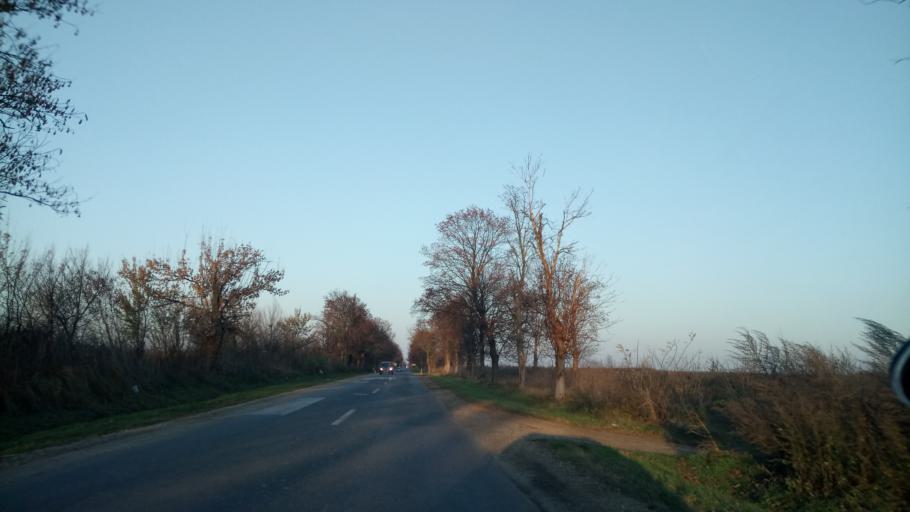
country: RS
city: Novi Slankamen
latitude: 45.1090
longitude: 20.2170
